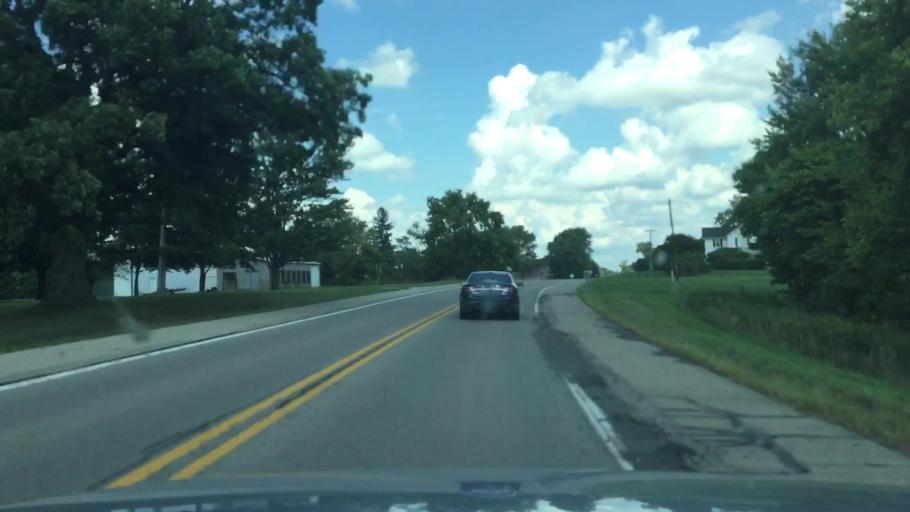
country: US
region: Michigan
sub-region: Lenawee County
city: Clinton
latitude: 42.1062
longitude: -83.8948
